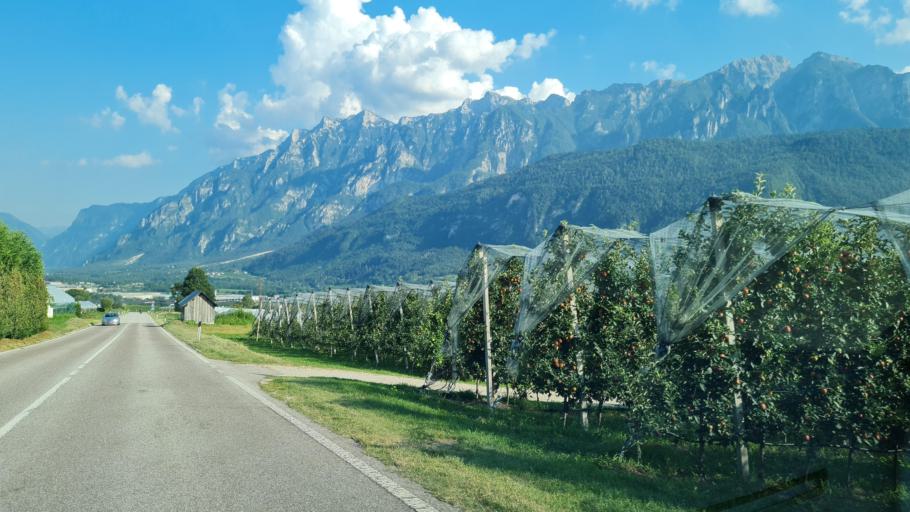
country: IT
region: Trentino-Alto Adige
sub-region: Provincia di Trento
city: Telve
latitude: 46.0639
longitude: 11.4861
